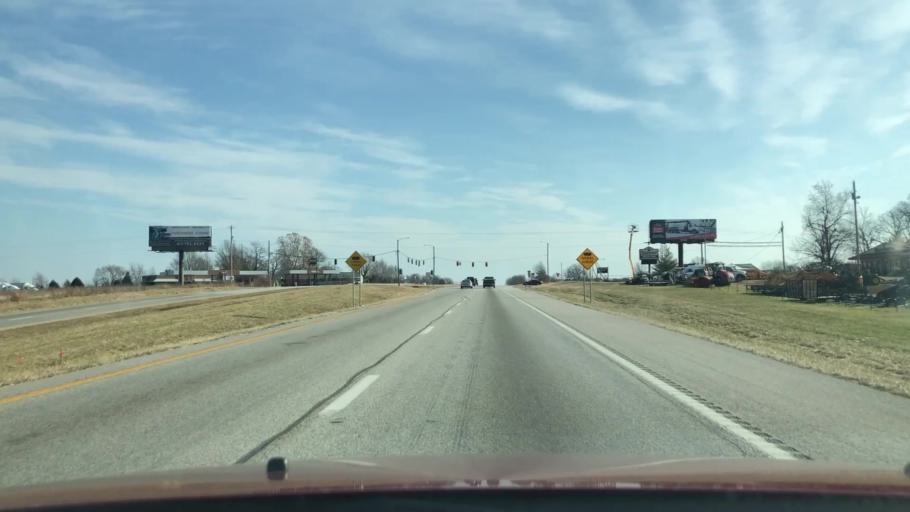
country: US
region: Missouri
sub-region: Webster County
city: Rogersville
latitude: 37.1187
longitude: -93.1217
